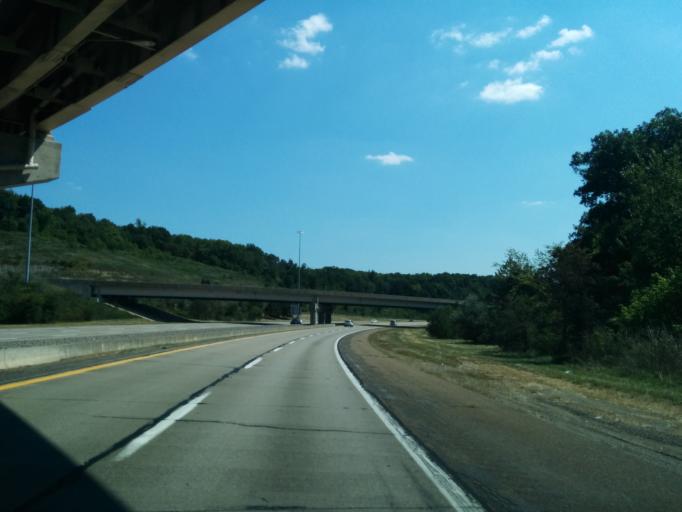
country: US
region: Pennsylvania
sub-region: Allegheny County
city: Enlow
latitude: 40.4678
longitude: -80.2003
